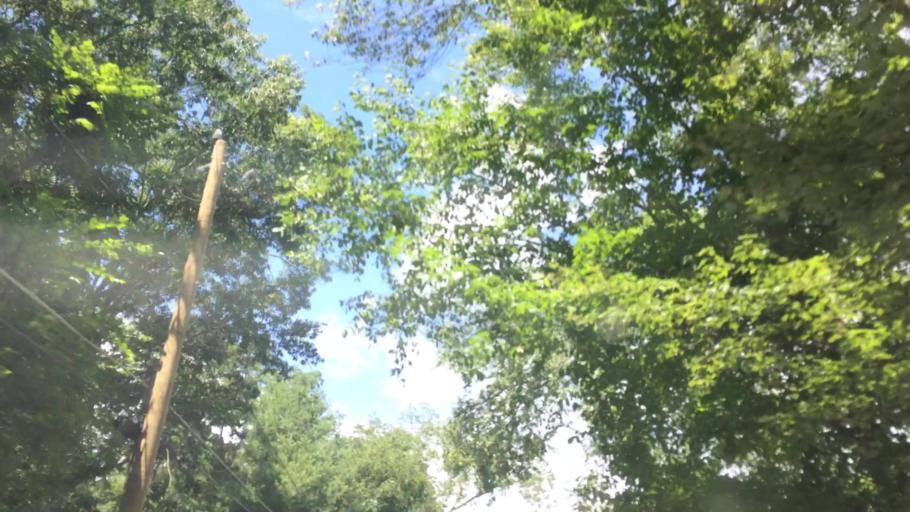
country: US
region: Massachusetts
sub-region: Middlesex County
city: Sudbury
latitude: 42.3779
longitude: -71.4027
